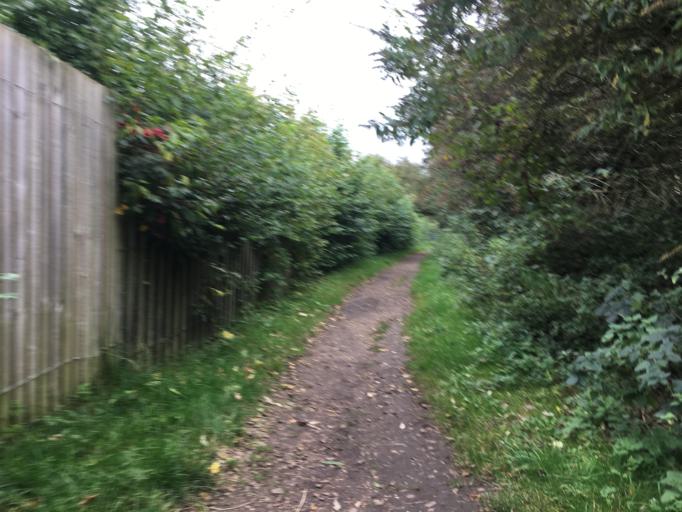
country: GB
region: England
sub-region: Warwickshire
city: Rugby
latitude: 52.3693
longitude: -1.2360
